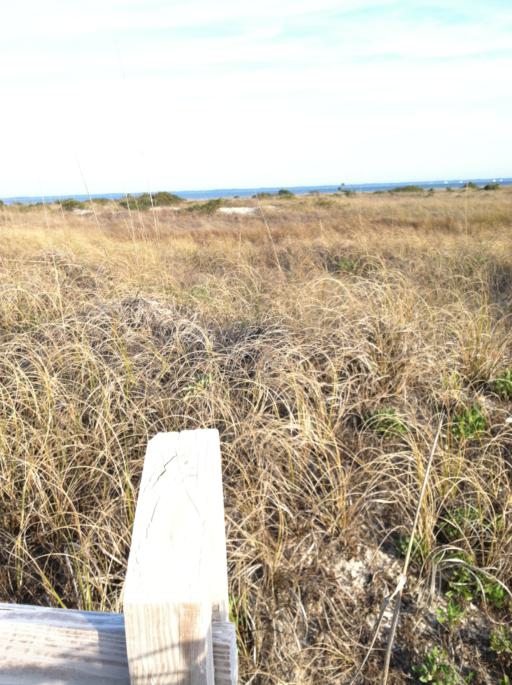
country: US
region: Florida
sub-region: Franklin County
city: Carrabelle
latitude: 29.7302
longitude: -84.7316
